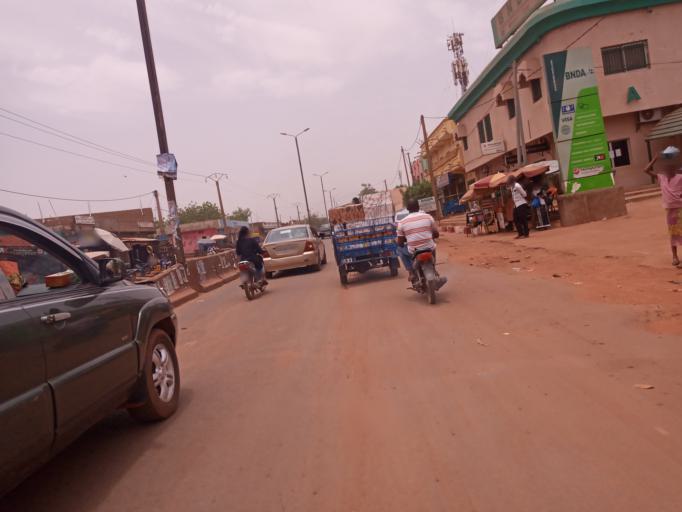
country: ML
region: Bamako
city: Bamako
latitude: 12.5958
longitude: -8.0163
